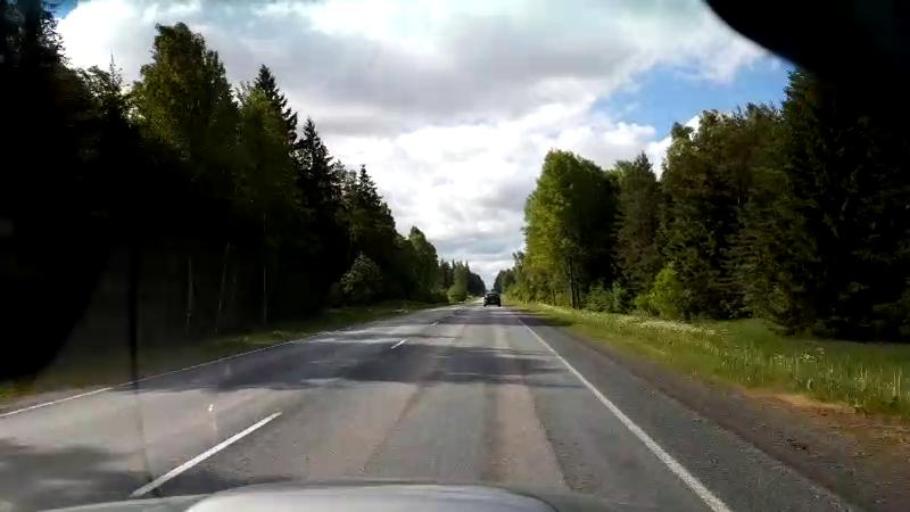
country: EE
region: Harju
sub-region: Saue linn
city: Saue
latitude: 59.2137
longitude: 24.4958
